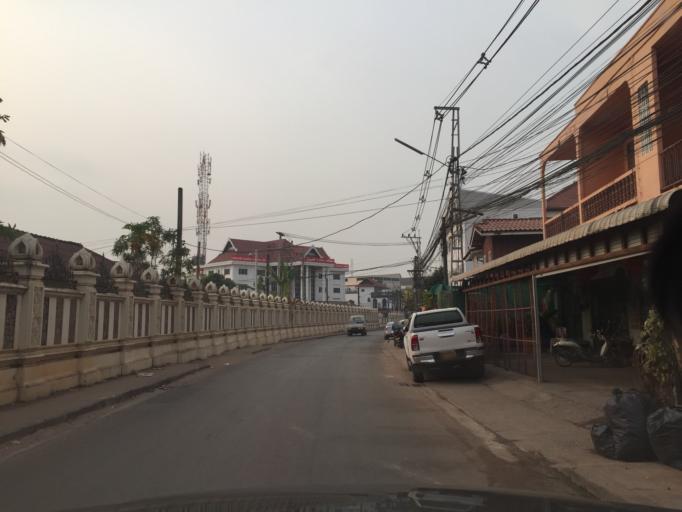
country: LA
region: Vientiane
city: Vientiane
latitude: 17.9737
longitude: 102.6165
